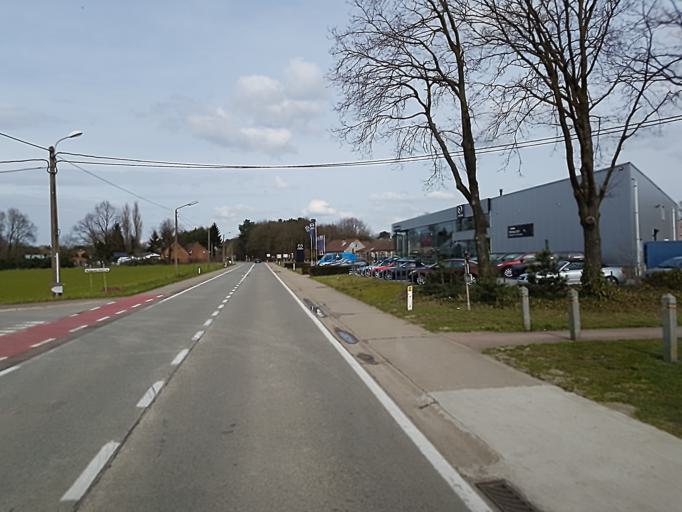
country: BE
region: Flanders
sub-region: Provincie Antwerpen
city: Meerhout
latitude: 51.1433
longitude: 5.0866
